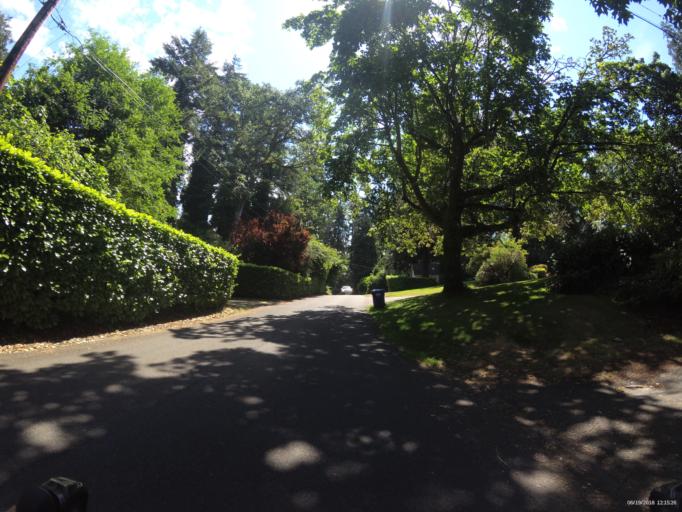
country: US
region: Washington
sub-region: Pierce County
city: Lakewood
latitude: 47.1726
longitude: -122.5337
